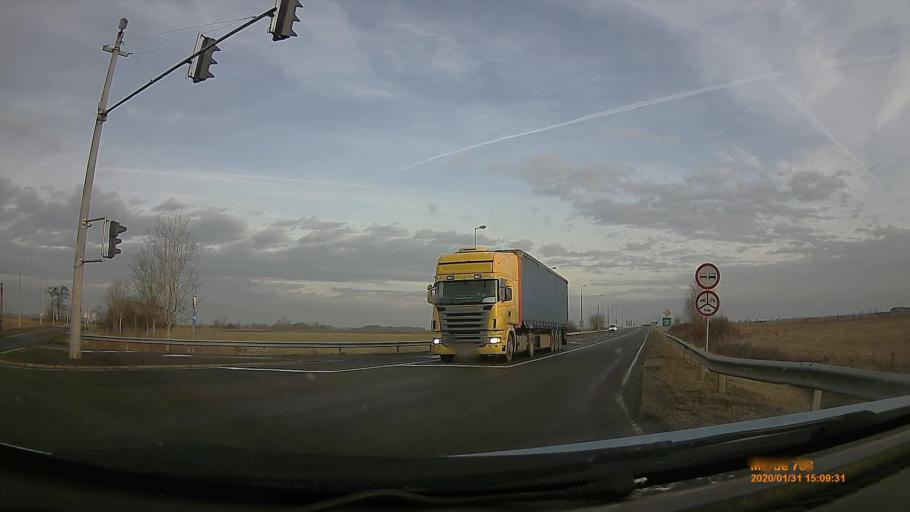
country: HU
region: Hajdu-Bihar
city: Polgar
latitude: 47.8692
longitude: 21.1440
